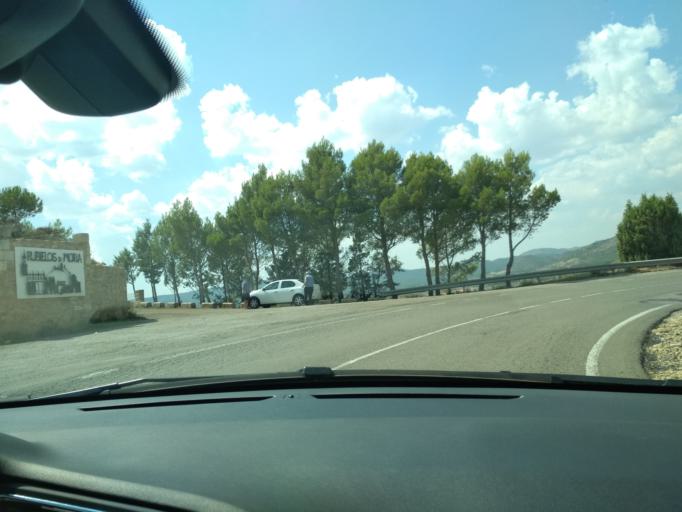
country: ES
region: Aragon
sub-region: Provincia de Teruel
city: Rubielos de Mora
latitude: 40.1869
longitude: -0.6508
